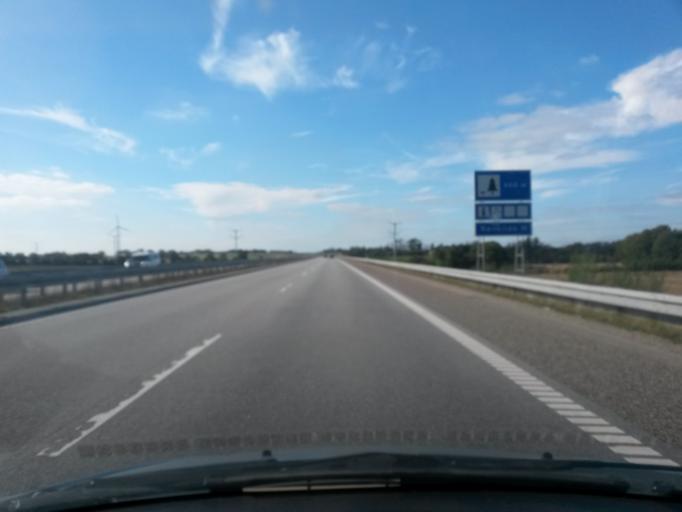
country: DK
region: Central Jutland
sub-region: Ikast-Brande Kommune
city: Bording Kirkeby
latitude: 56.1330
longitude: 9.3179
